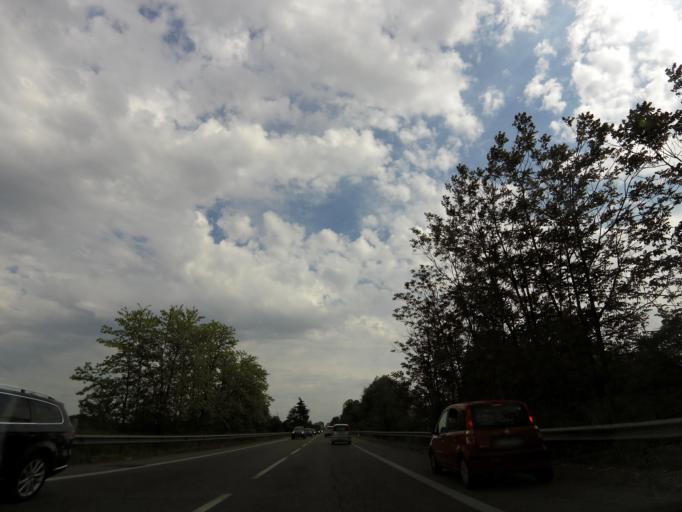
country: IT
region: Lombardy
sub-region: Citta metropolitana di Milano
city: Melegnano
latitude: 45.3746
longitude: 9.3083
